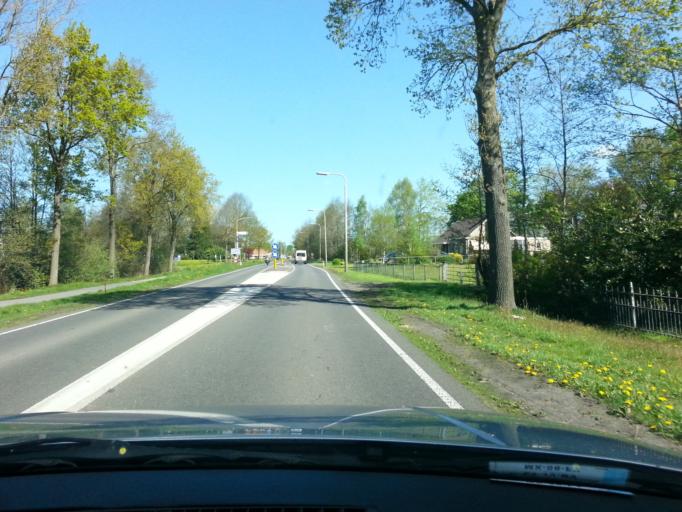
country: NL
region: Friesland
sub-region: Gemeente Achtkarspelen
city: Surhuizum
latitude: 53.1954
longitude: 6.1847
